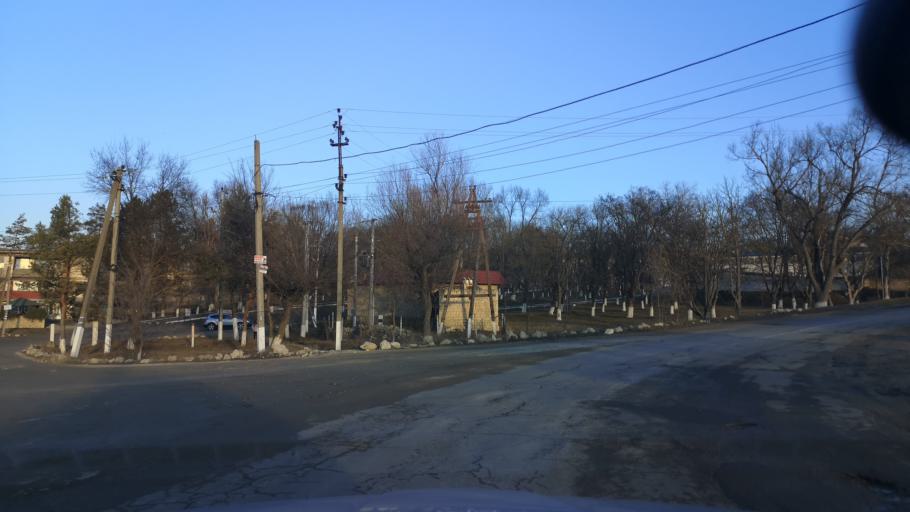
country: MD
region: Orhei
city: Orhei
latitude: 47.3096
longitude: 28.9318
